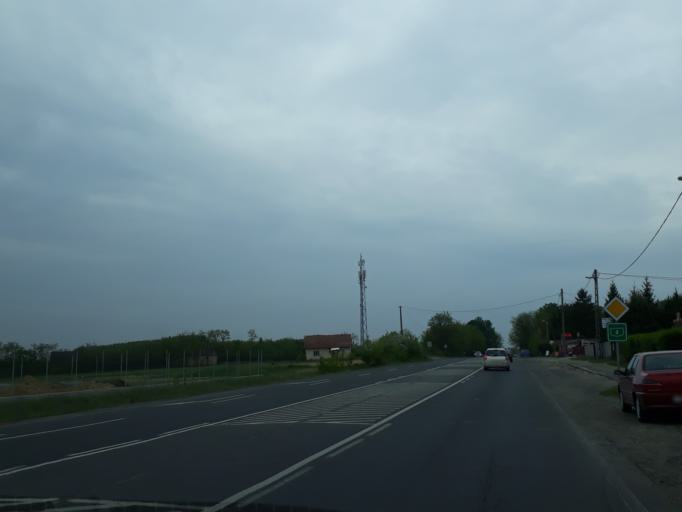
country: HU
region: Szabolcs-Szatmar-Bereg
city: Nyirpazony
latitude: 47.9808
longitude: 21.7802
